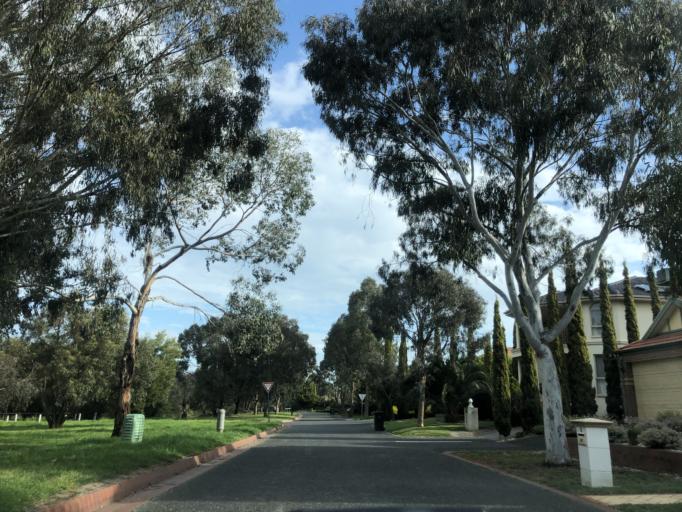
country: AU
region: Victoria
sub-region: Monash
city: Notting Hill
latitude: -37.8962
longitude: 145.1526
